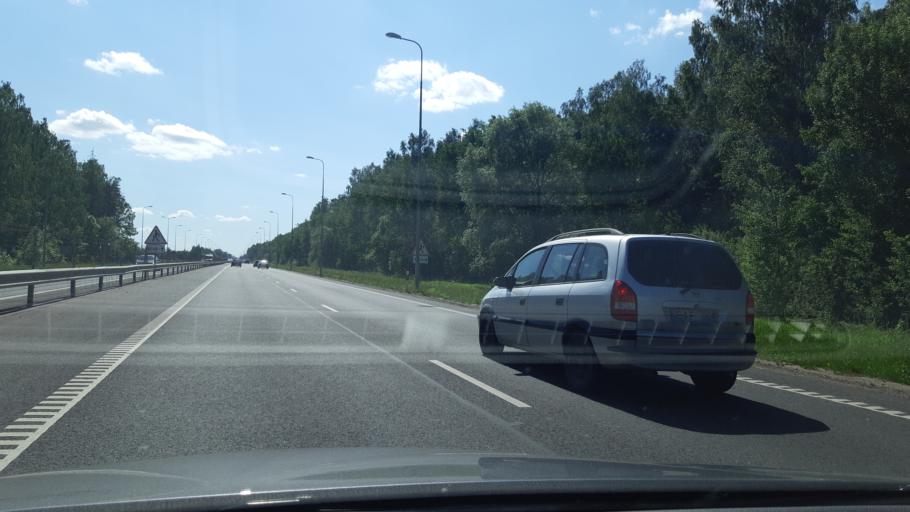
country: LT
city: Ramuciai
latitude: 54.9531
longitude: 24.0272
